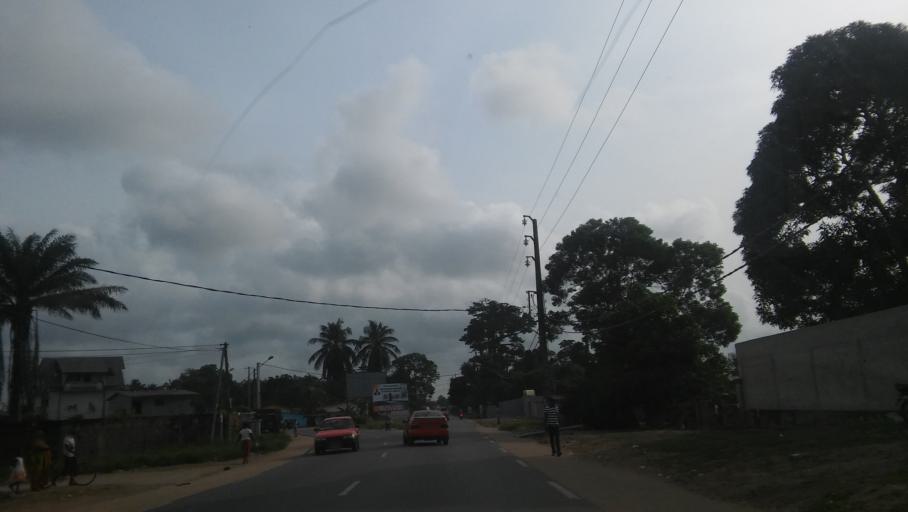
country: CI
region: Sud-Comoe
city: Grand-Bassam
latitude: 5.2161
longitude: -3.7299
